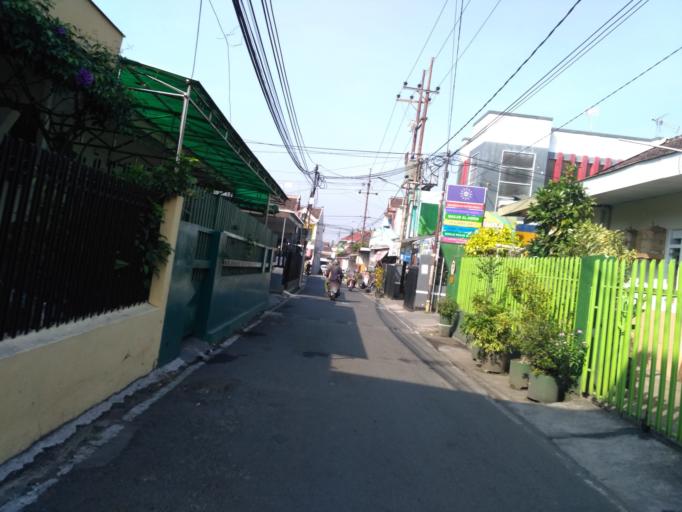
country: ID
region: East Java
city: Malang
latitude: -7.9787
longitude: 112.6207
